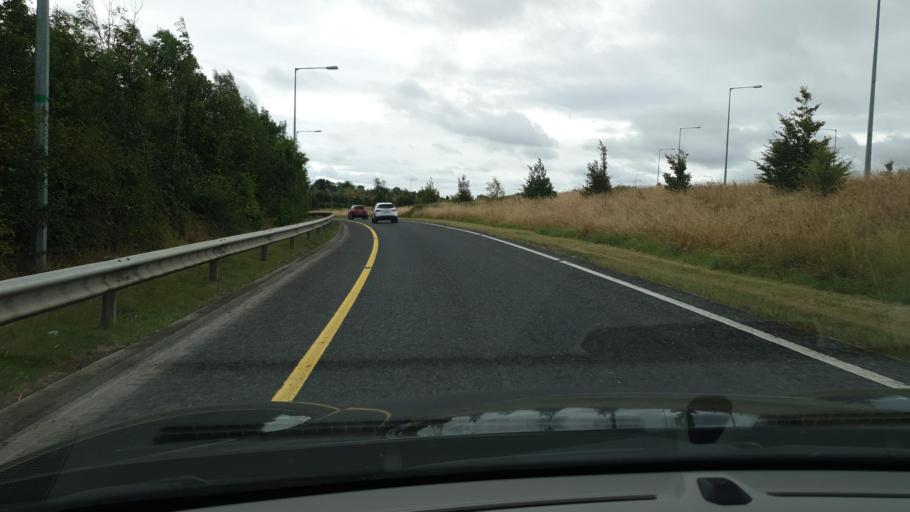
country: IE
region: Leinster
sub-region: An Mhi
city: Ashbourne
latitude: 53.4899
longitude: -6.3848
